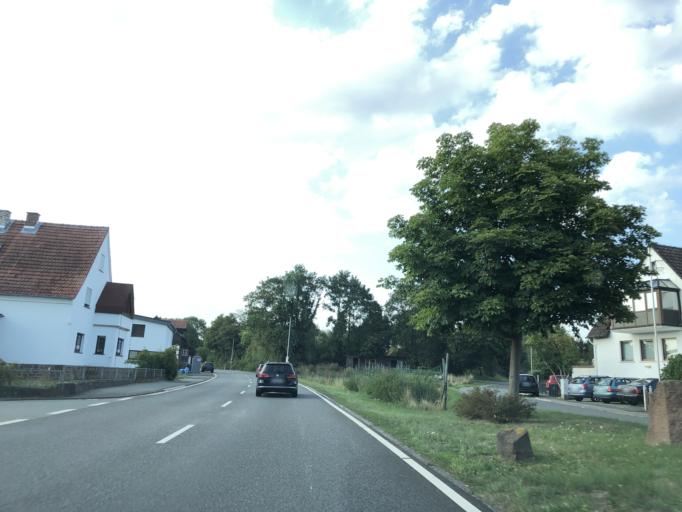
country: DE
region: Hesse
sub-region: Regierungsbezirk Giessen
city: Munchhausen
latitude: 50.9638
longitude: 8.7158
